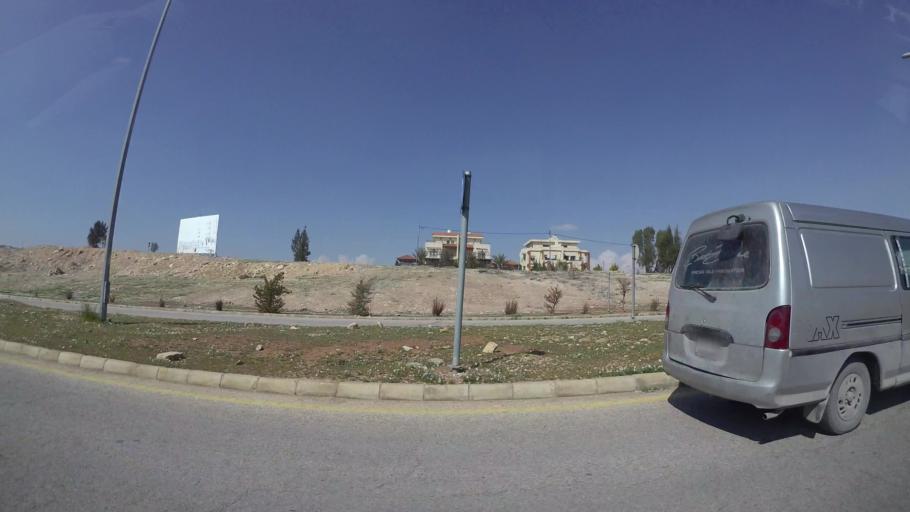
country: JO
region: Zarqa
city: Zarqa
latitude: 32.0731
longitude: 36.1060
